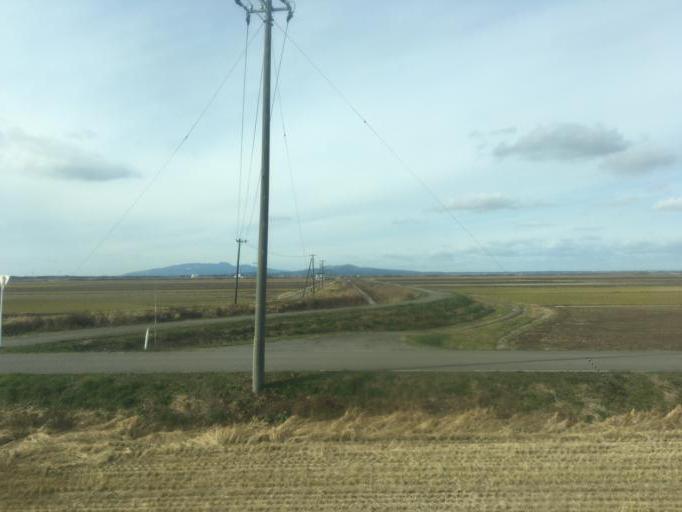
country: JP
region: Akita
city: Tenno
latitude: 39.8896
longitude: 140.0698
